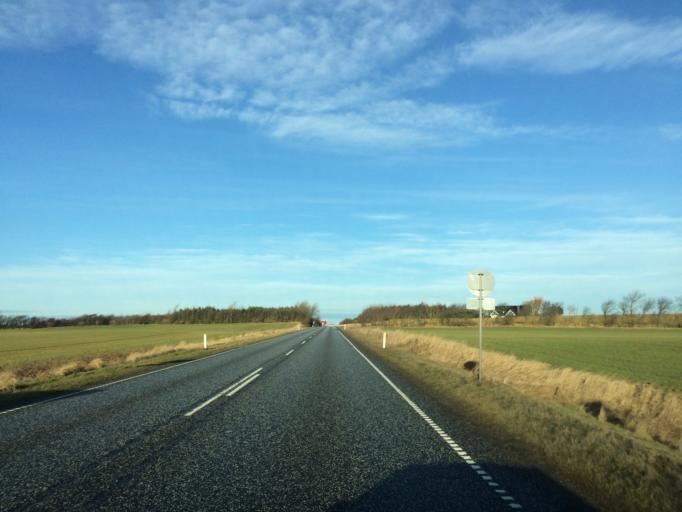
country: DK
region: Central Jutland
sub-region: Struer Kommune
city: Struer
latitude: 56.5422
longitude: 8.5603
